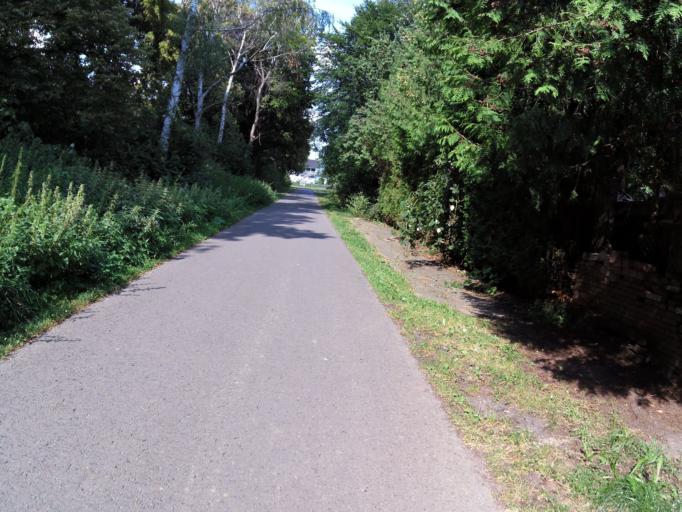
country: DE
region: North Rhine-Westphalia
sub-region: Regierungsbezirk Detmold
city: Minden
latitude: 52.2991
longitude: 8.9275
